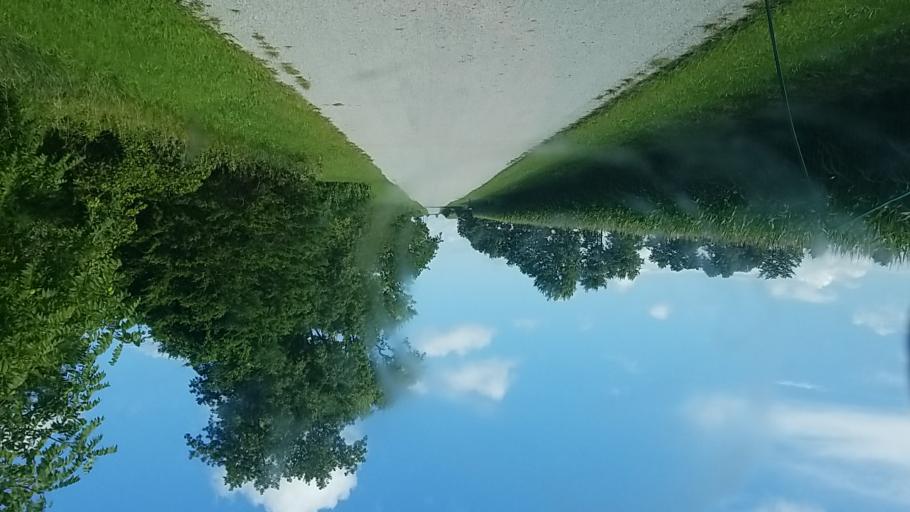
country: US
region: Ohio
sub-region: Hardin County
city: Kenton
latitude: 40.6752
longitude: -83.5475
